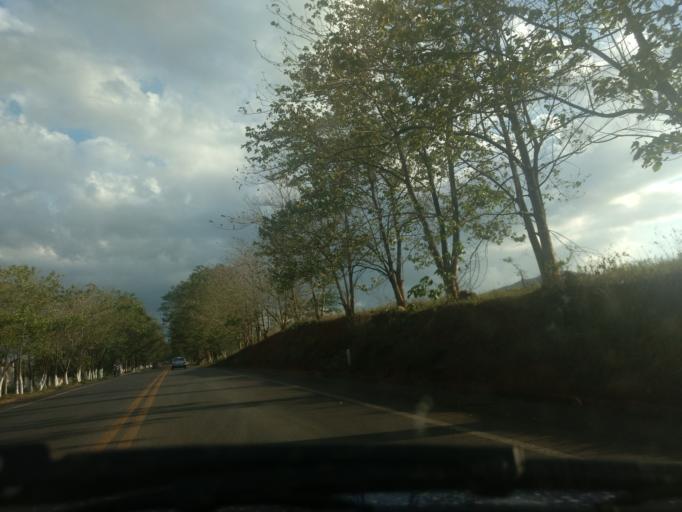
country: MX
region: Nayarit
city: Puga
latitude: 21.5235
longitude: -104.8123
